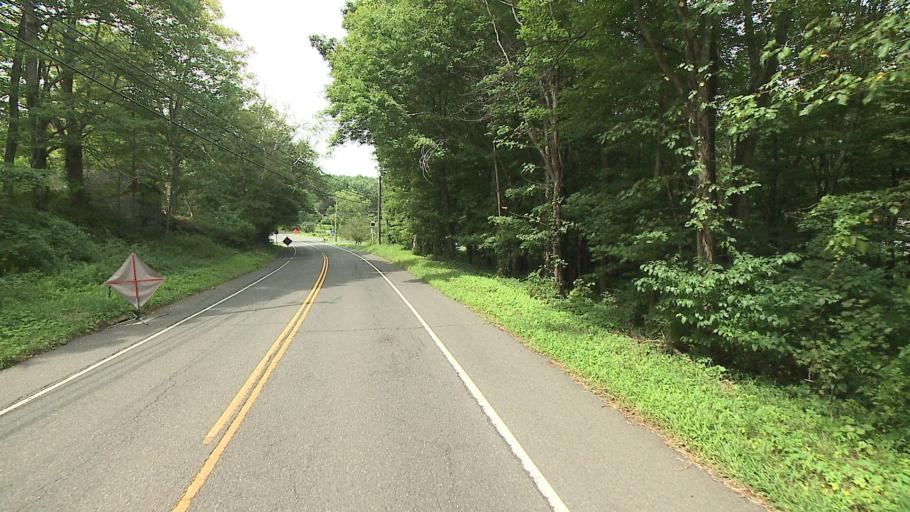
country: US
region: Connecticut
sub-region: Litchfield County
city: Woodbury
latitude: 41.5624
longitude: -73.3007
